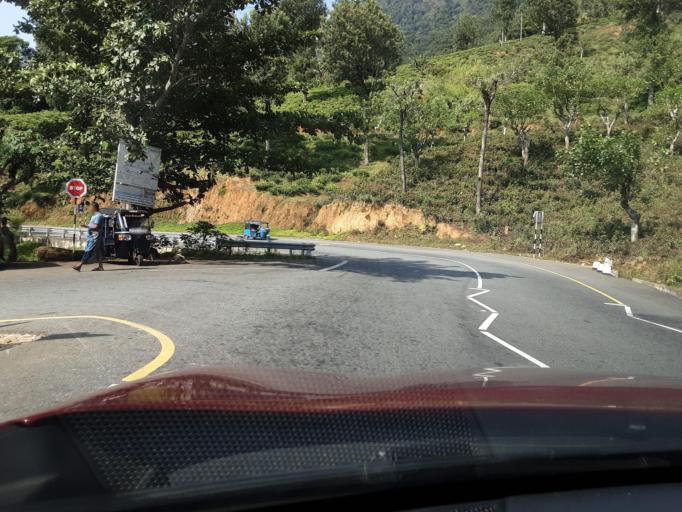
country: LK
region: Uva
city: Badulla
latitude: 6.9526
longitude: 81.1224
